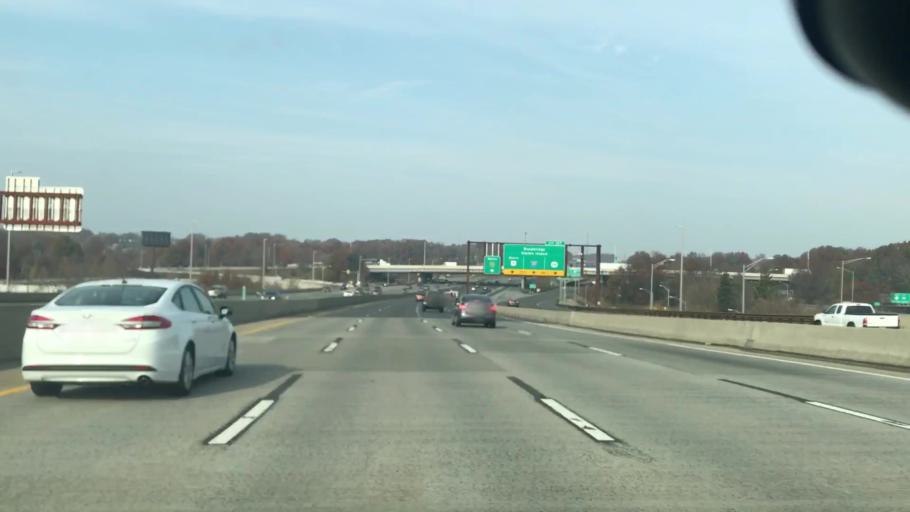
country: US
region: New Jersey
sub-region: Middlesex County
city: Fords
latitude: 40.5154
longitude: -74.3010
